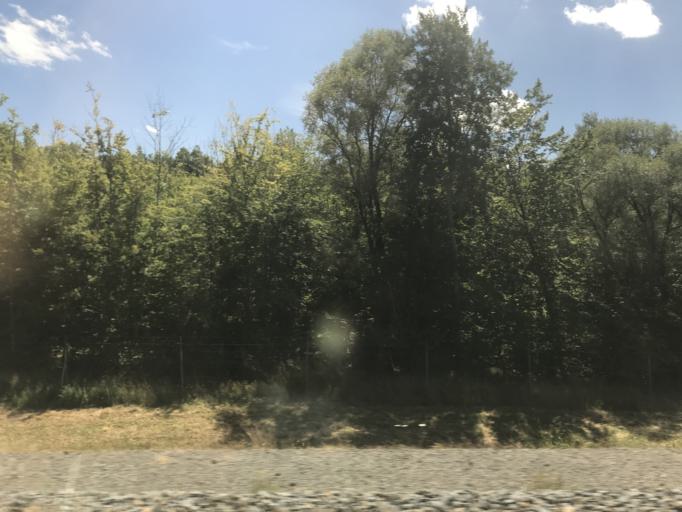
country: FR
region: Lorraine
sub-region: Departement de la Moselle
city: Solgne
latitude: 48.9597
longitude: 6.3145
